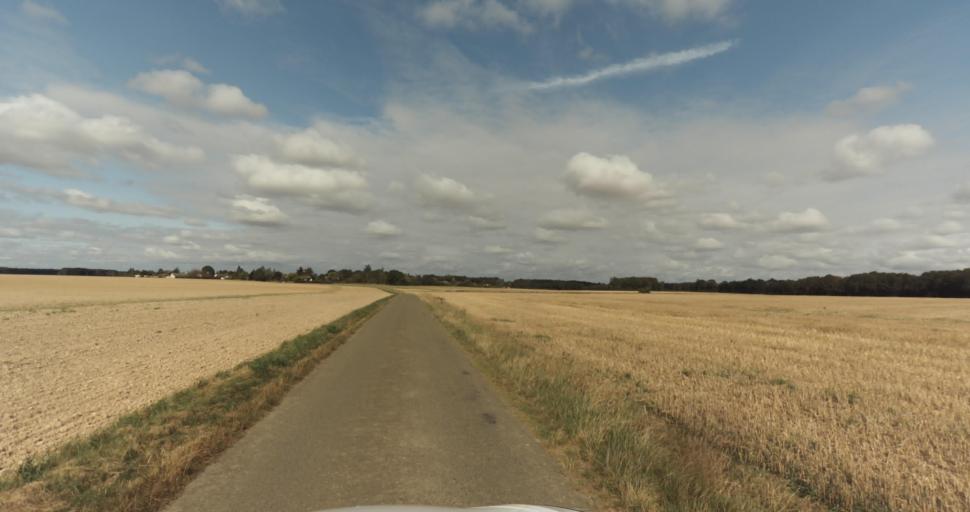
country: FR
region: Haute-Normandie
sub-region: Departement de l'Eure
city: Tillieres-sur-Avre
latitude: 48.7566
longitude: 1.1183
